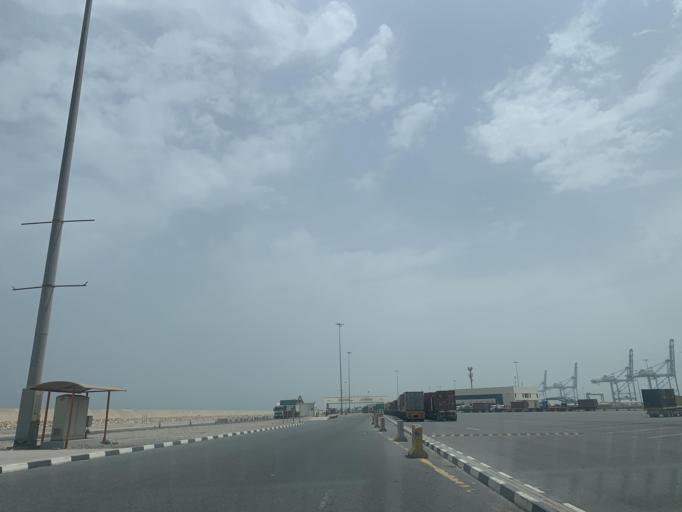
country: BH
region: Muharraq
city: Al Hadd
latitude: 26.1971
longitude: 50.7121
